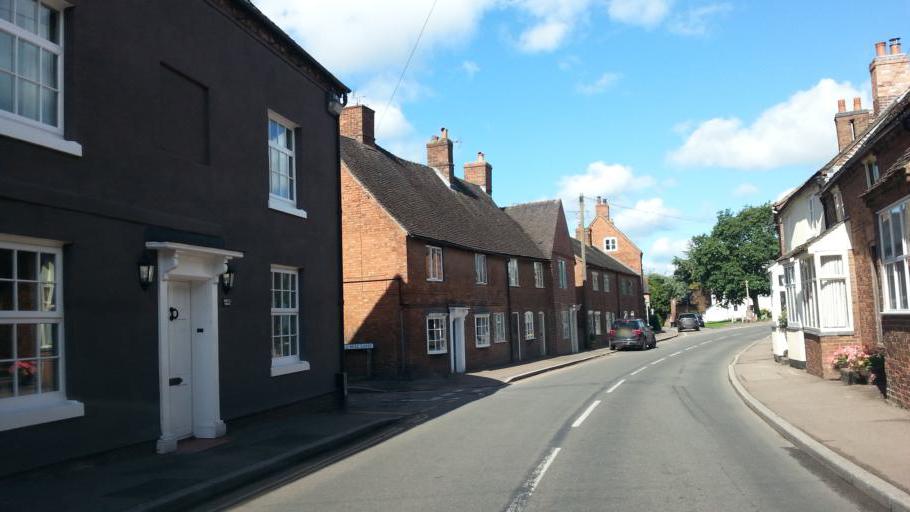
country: GB
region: England
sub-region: Staffordshire
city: Armitage
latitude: 52.8180
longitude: -1.8806
